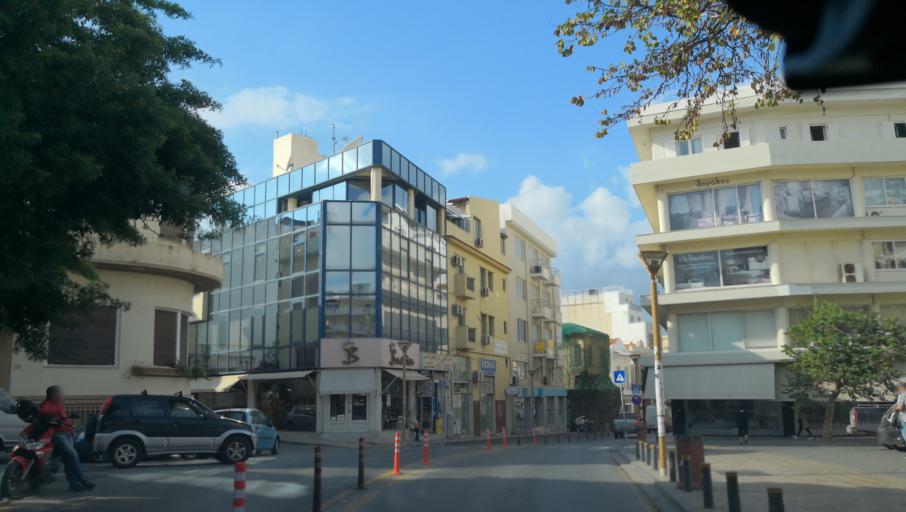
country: GR
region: Crete
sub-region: Nomos Irakleiou
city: Irakleion
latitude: 35.3372
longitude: 25.1305
